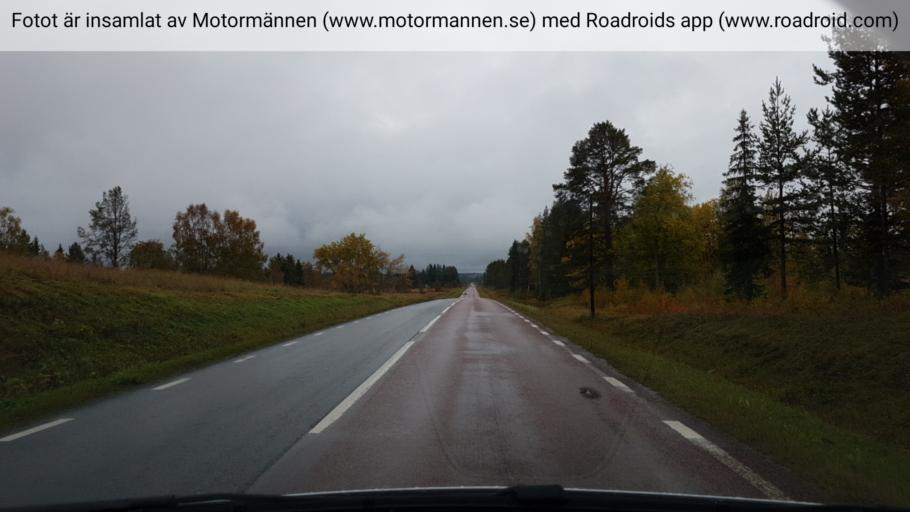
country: SE
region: Jaemtland
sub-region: Stroemsunds Kommun
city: Stroemsund
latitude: 63.7722
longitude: 15.5052
